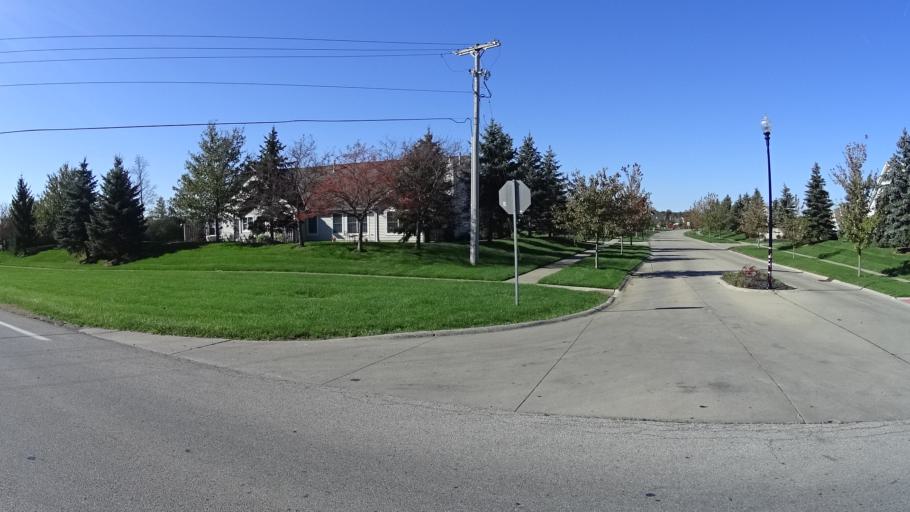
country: US
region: Ohio
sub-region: Lorain County
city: Oberlin
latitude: 41.2741
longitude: -82.2173
